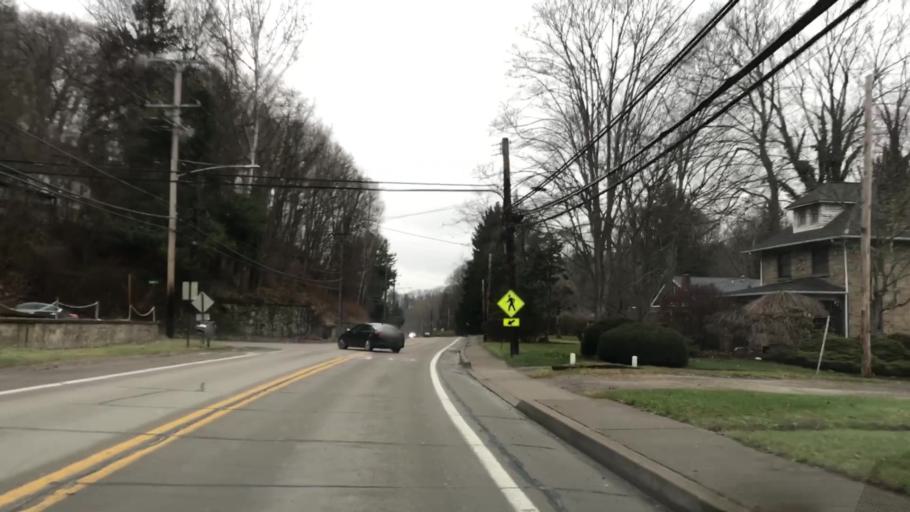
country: US
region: Pennsylvania
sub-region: Allegheny County
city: Leetsdale
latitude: 40.5462
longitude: -80.2186
